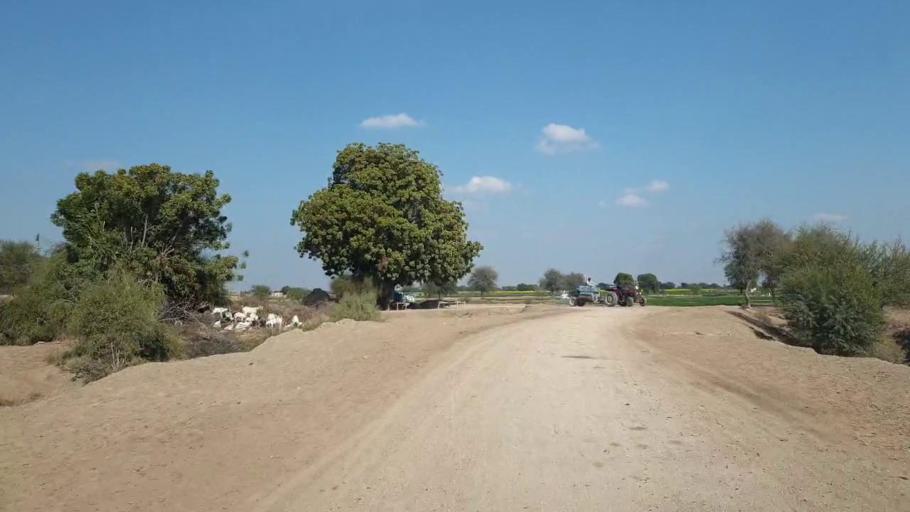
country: PK
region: Sindh
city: Shahpur Chakar
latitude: 26.0876
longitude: 68.5828
